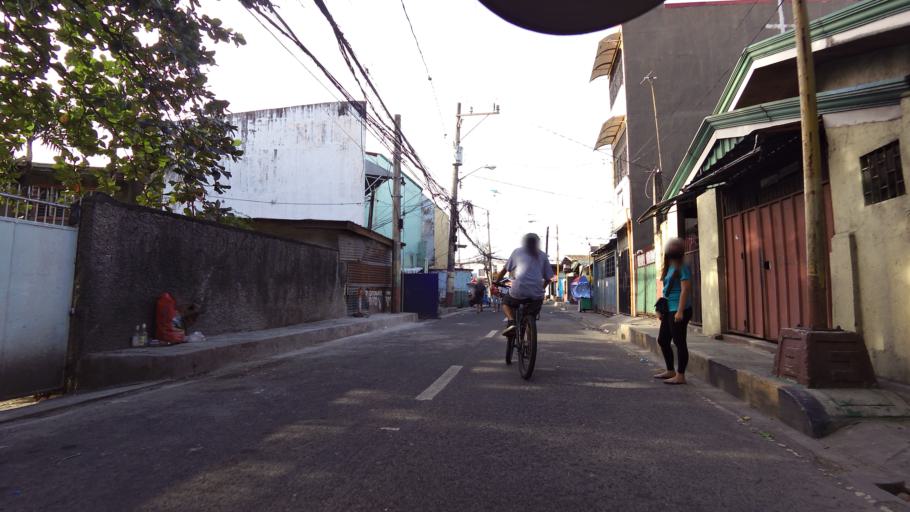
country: PH
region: Calabarzon
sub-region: Province of Rizal
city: Pateros
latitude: 14.5653
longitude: 121.0837
